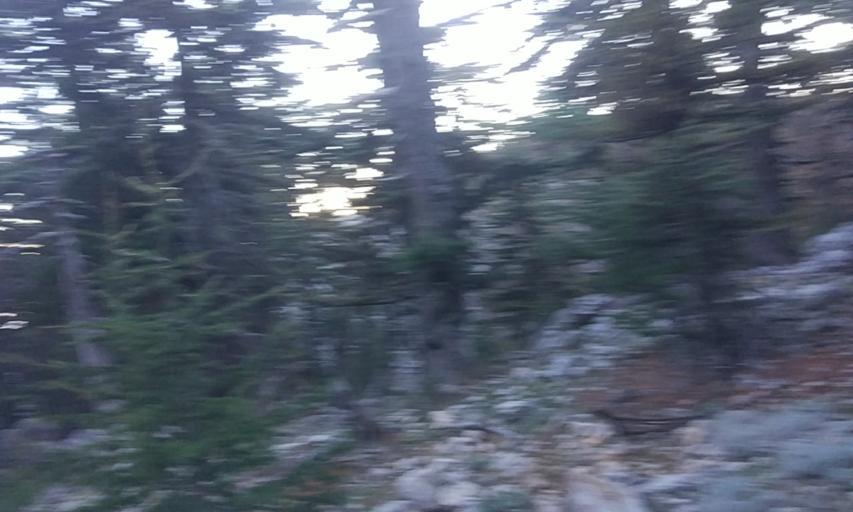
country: TR
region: Antalya
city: Altinyaka
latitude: 36.5378
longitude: 30.4167
